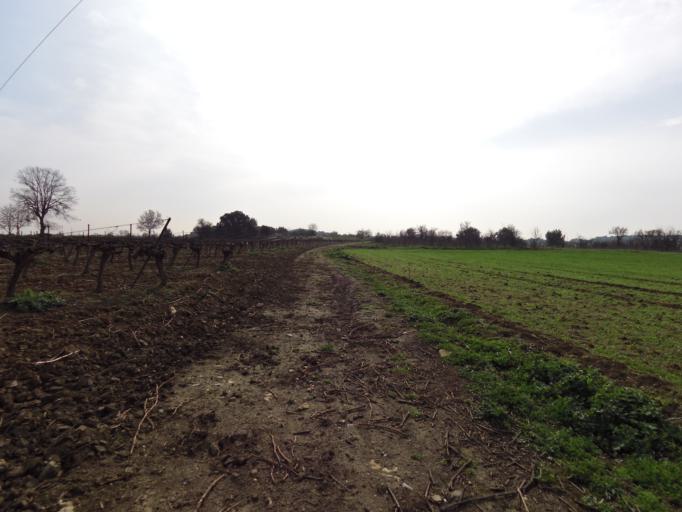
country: FR
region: Languedoc-Roussillon
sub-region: Departement du Gard
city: Aigues-Vives
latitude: 43.7505
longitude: 4.1890
